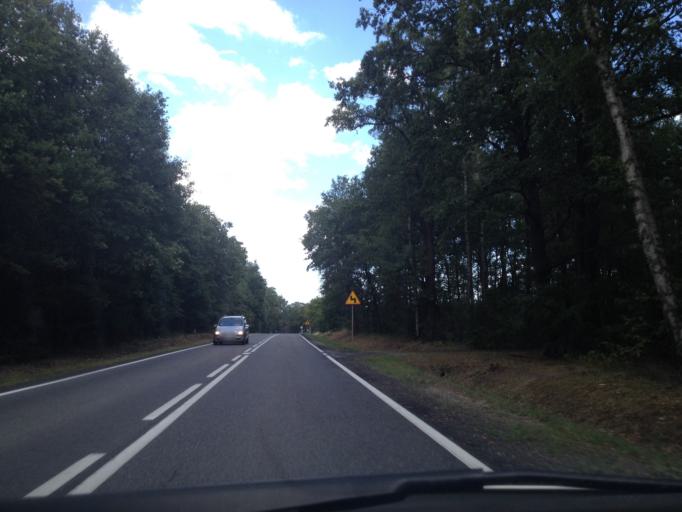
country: PL
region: Lubusz
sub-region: Powiat zarski
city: Sieniawa Zarska
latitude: 51.5817
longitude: 15.0715
